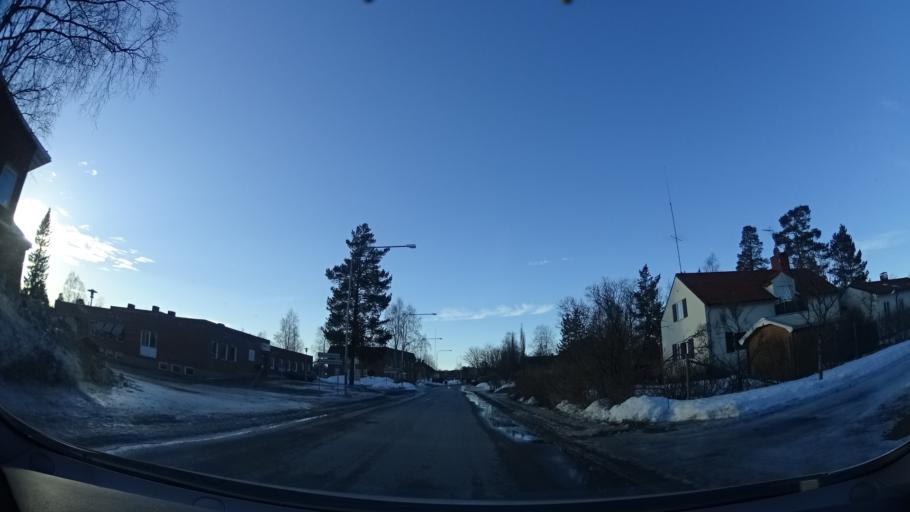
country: SE
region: Vaesterbotten
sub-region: Skelleftea Kommun
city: Byske
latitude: 64.9505
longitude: 21.2063
